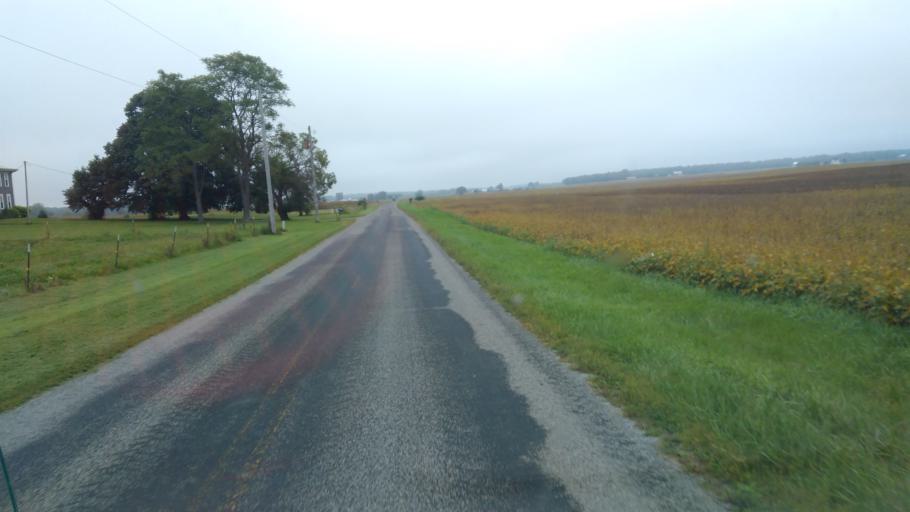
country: US
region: Ohio
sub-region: Hardin County
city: Kenton
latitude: 40.5353
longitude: -83.6312
